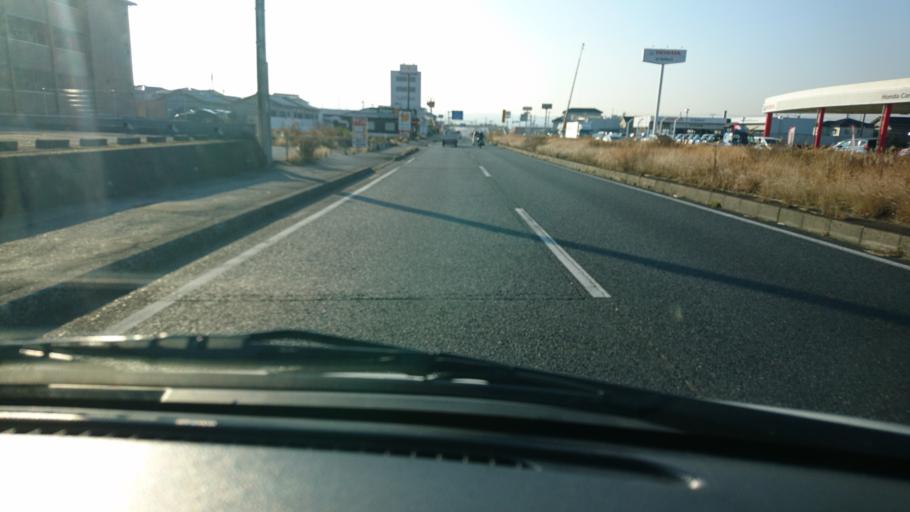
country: JP
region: Chiba
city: Kimitsu
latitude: 35.3314
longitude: 139.9235
